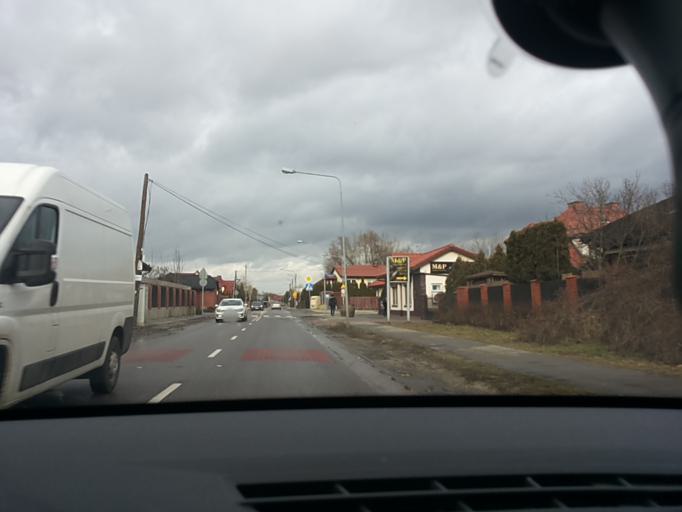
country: PL
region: Masovian Voivodeship
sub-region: Warszawa
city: Targowek
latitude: 52.3083
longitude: 21.0521
